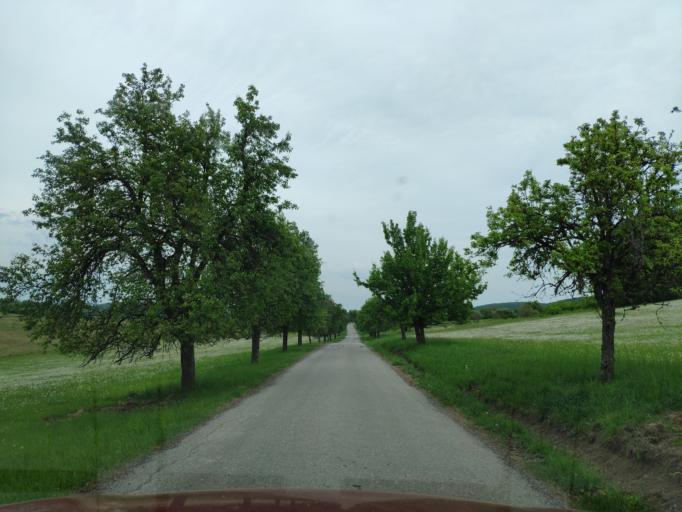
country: SK
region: Banskobystricky
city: Revuca
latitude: 48.5242
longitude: 20.1227
